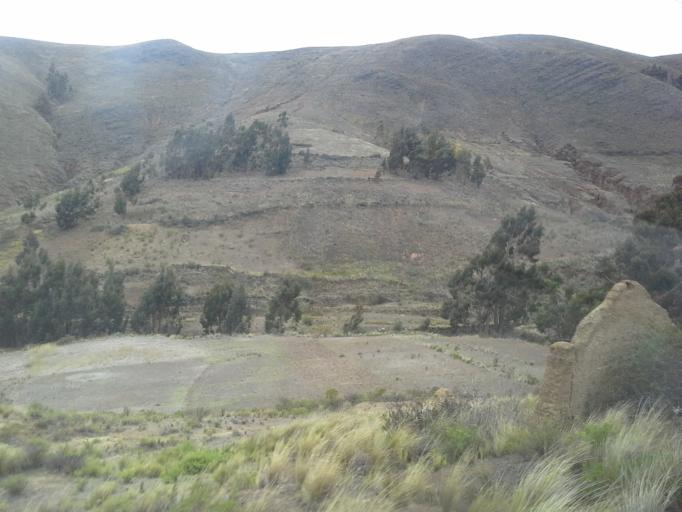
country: BO
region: Cochabamba
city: Colomi
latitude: -17.4143
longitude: -65.8045
